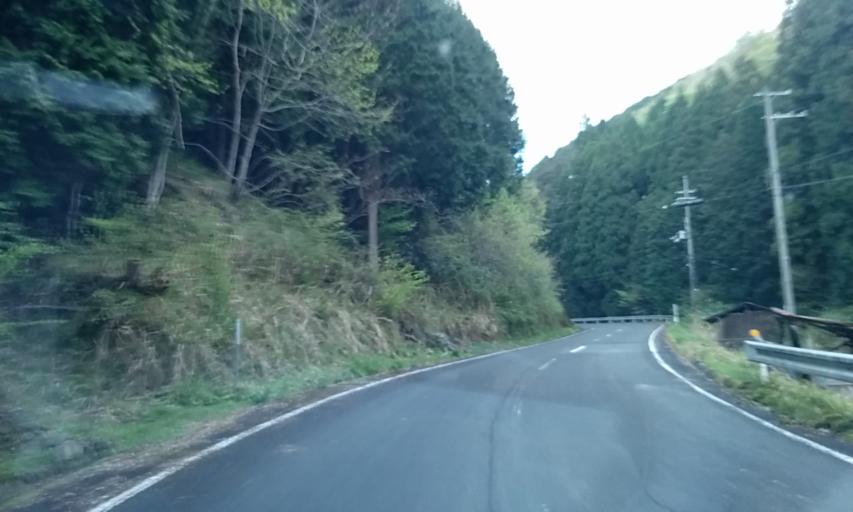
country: JP
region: Kyoto
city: Ayabe
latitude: 35.2536
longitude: 135.3121
